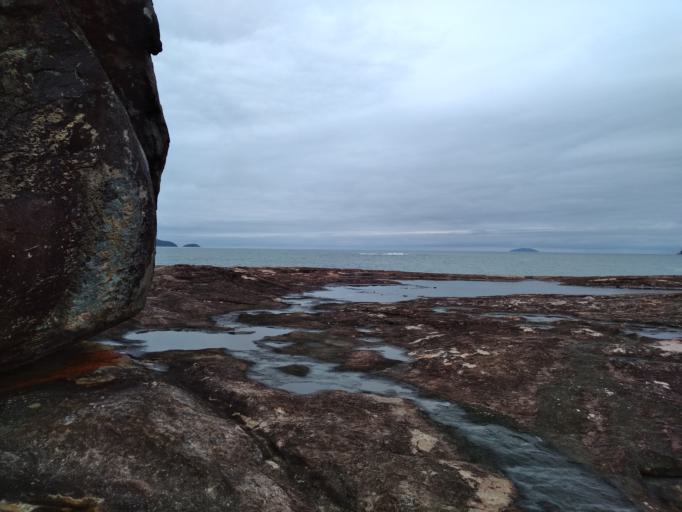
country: BR
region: Sao Paulo
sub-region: Ubatuba
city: Ubatuba
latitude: -23.5299
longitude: -45.1584
